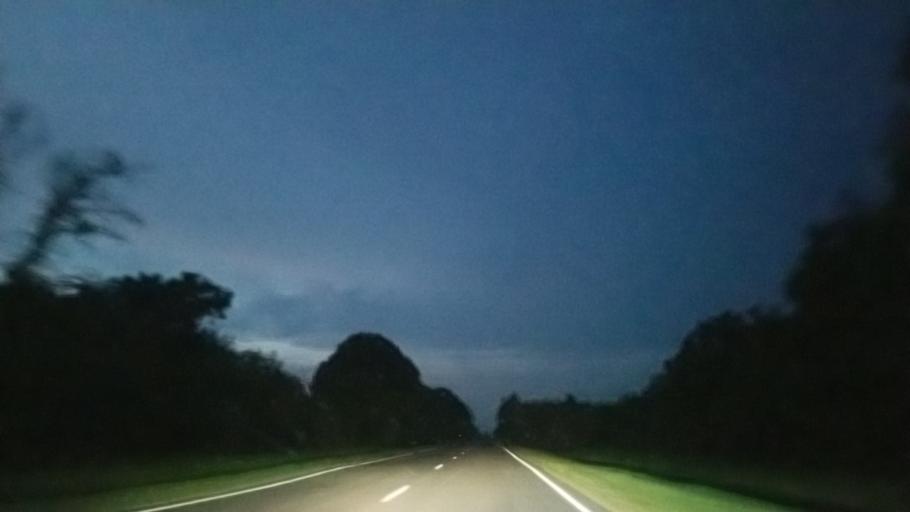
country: PL
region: Lublin Voivodeship
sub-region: Powiat bialski
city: Koden
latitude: 51.9090
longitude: 23.6561
